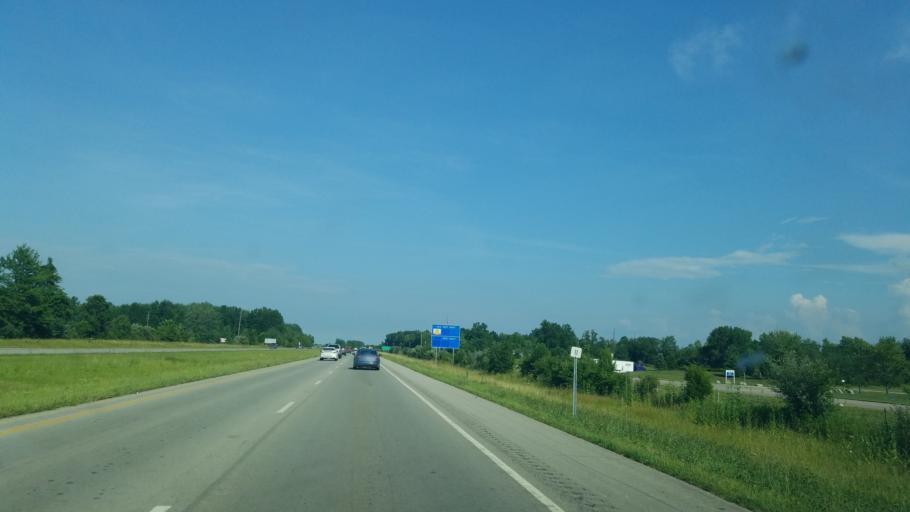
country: US
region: Ohio
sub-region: Clermont County
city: Batavia
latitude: 39.0739
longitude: -84.1140
